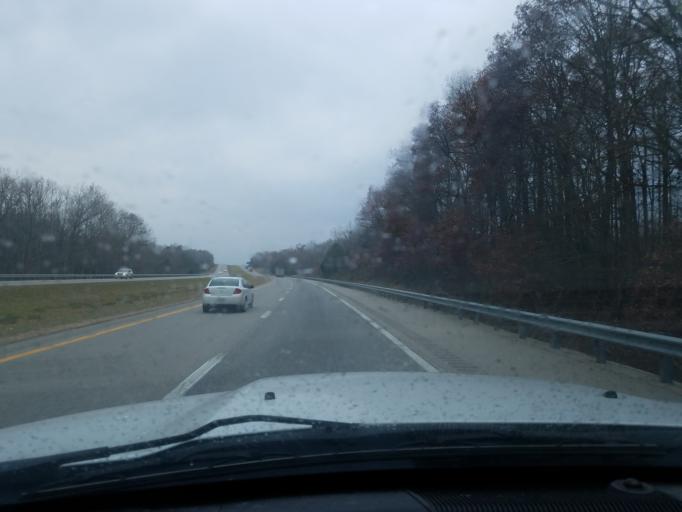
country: US
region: Kentucky
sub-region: Rowan County
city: Morehead
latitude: 38.1865
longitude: -83.5383
